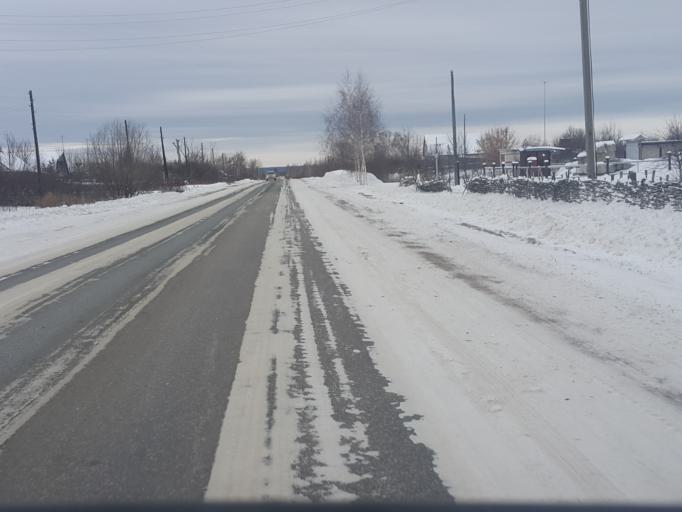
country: RU
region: Tambov
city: Platonovka
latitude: 52.8624
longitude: 41.8448
